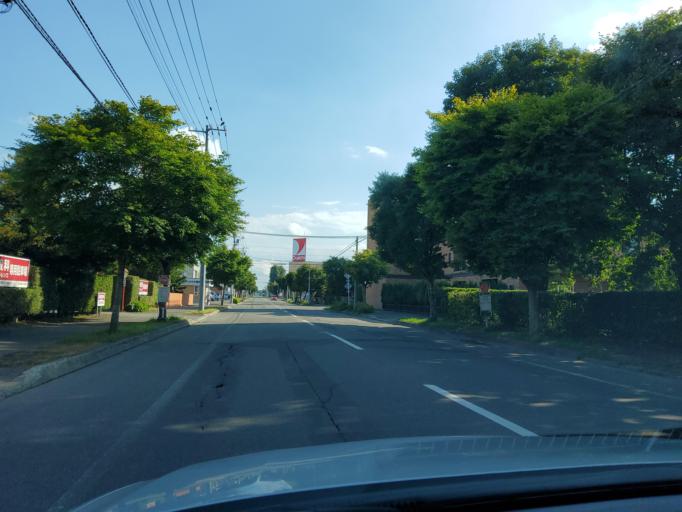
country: JP
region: Hokkaido
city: Obihiro
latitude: 42.9216
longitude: 143.2118
